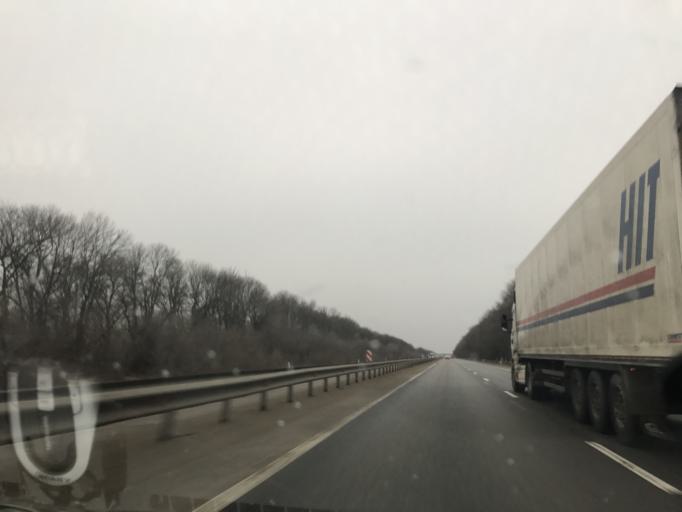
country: RU
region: Krasnodarskiy
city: Pavlovskaya
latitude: 46.1946
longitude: 39.8316
